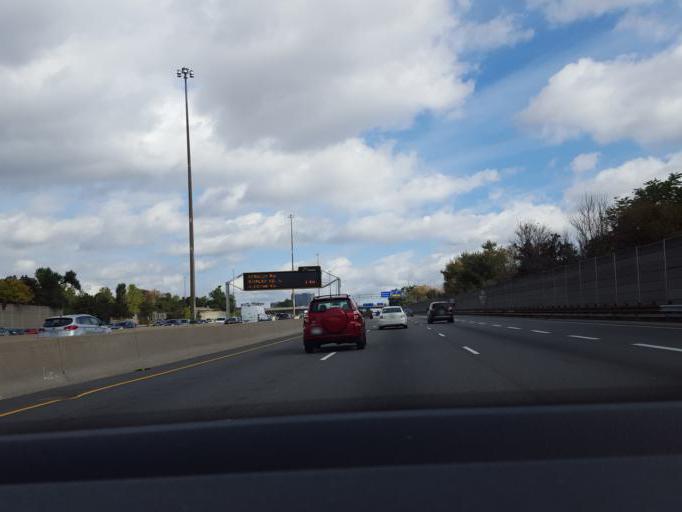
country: CA
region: Ontario
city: Scarborough
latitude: 43.7685
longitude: -79.3115
